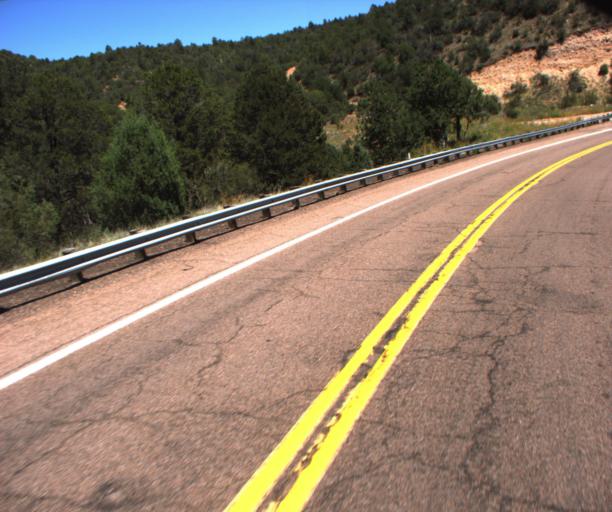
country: US
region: Arizona
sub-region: Navajo County
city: Cibecue
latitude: 33.9288
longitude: -110.3581
